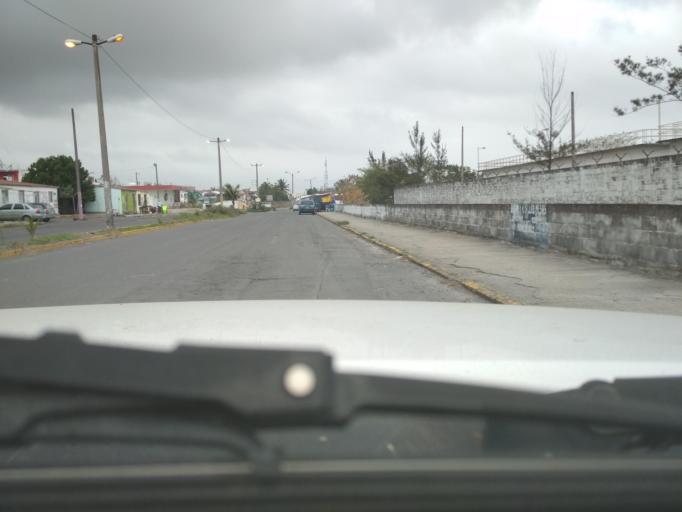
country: MX
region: Veracruz
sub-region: Veracruz
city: Fraccionamiento Geovillas los Pinos
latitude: 19.2158
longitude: -96.2245
